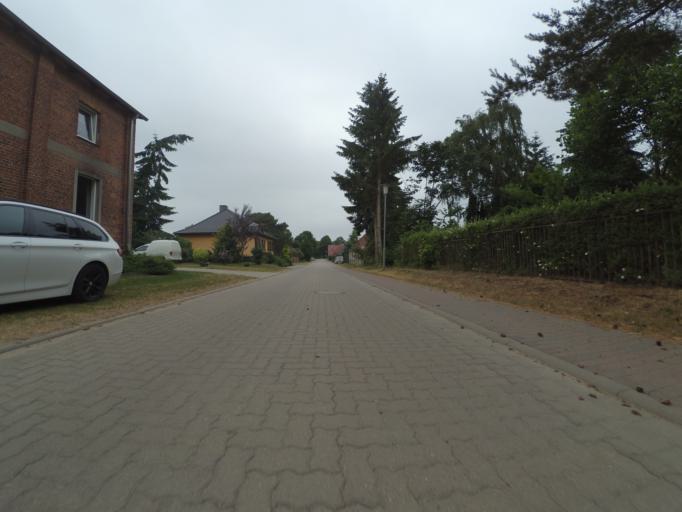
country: DE
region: Mecklenburg-Vorpommern
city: Goldberg
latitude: 53.5238
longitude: 12.1635
